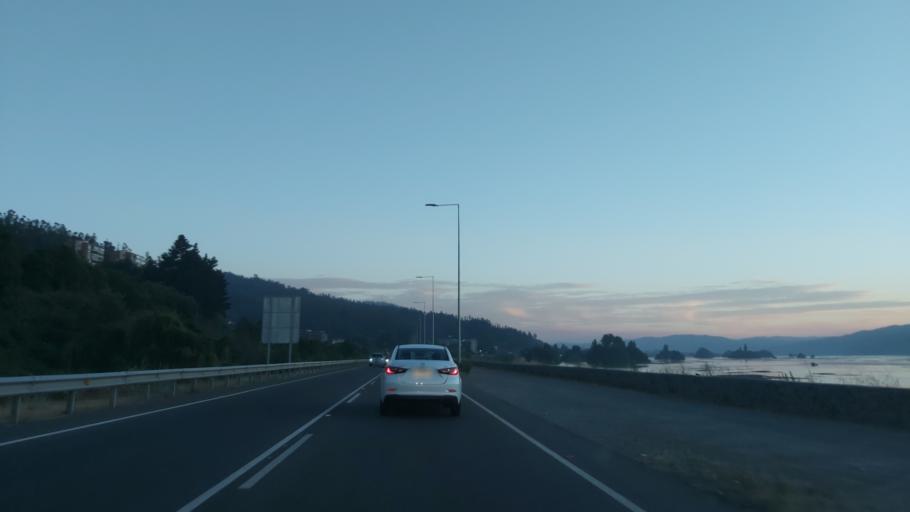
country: CL
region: Biobio
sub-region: Provincia de Concepcion
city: Concepcion
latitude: -36.8730
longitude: -73.0426
